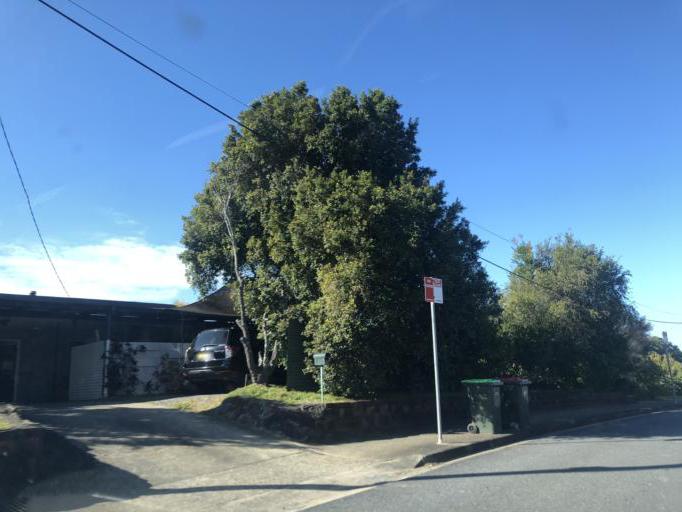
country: AU
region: New South Wales
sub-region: Coffs Harbour
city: Toormina
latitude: -30.3409
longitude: 153.0844
